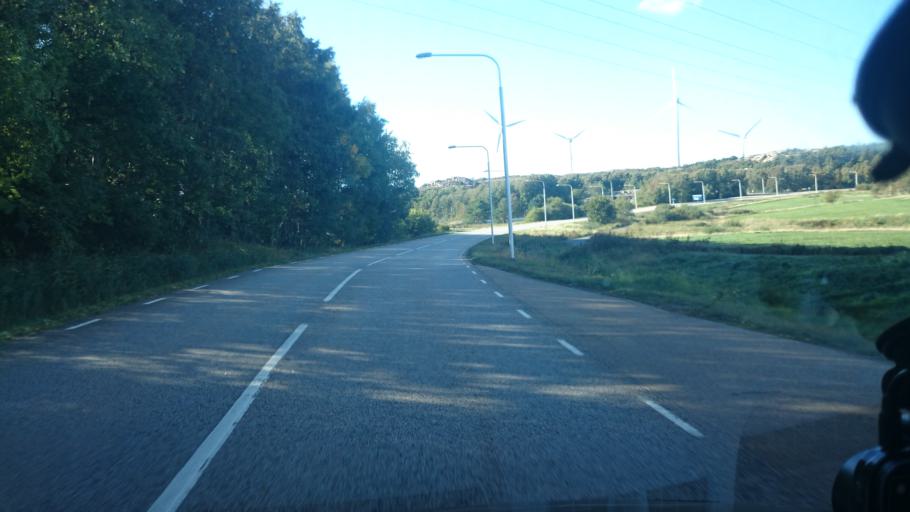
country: SE
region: Vaestra Goetaland
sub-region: Lysekils Kommun
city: Lysekil
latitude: 58.3352
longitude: 11.4250
